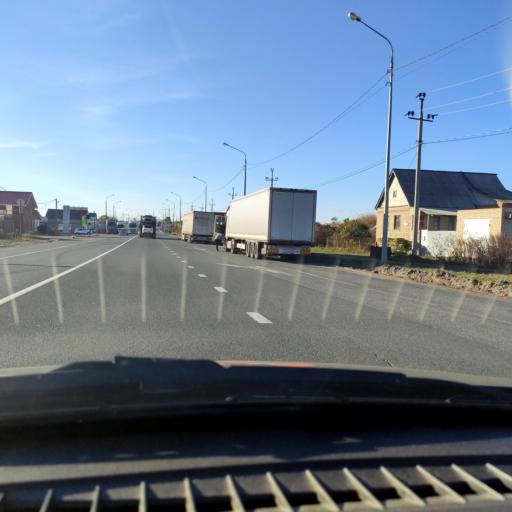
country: RU
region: Samara
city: Mezhdurechensk
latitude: 53.2483
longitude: 49.1741
